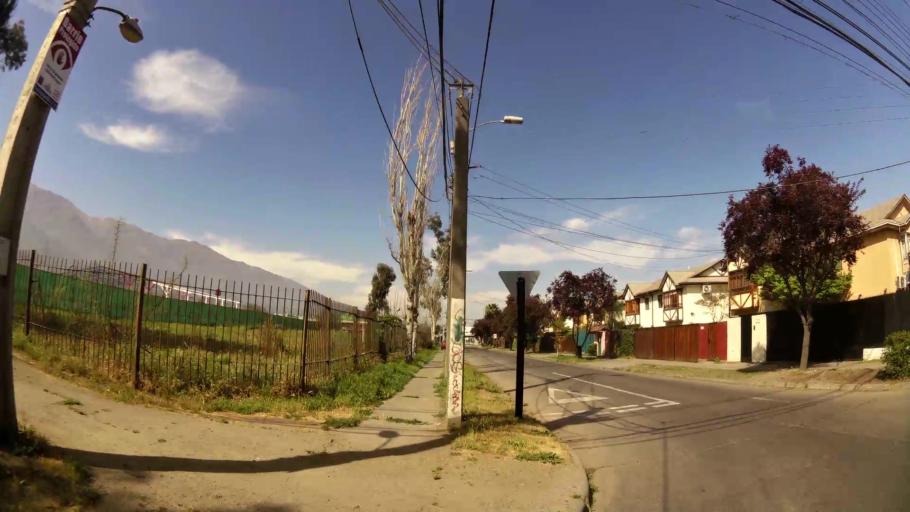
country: CL
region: Santiago Metropolitan
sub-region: Provincia de Santiago
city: Villa Presidente Frei, Nunoa, Santiago, Chile
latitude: -33.4502
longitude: -70.5413
